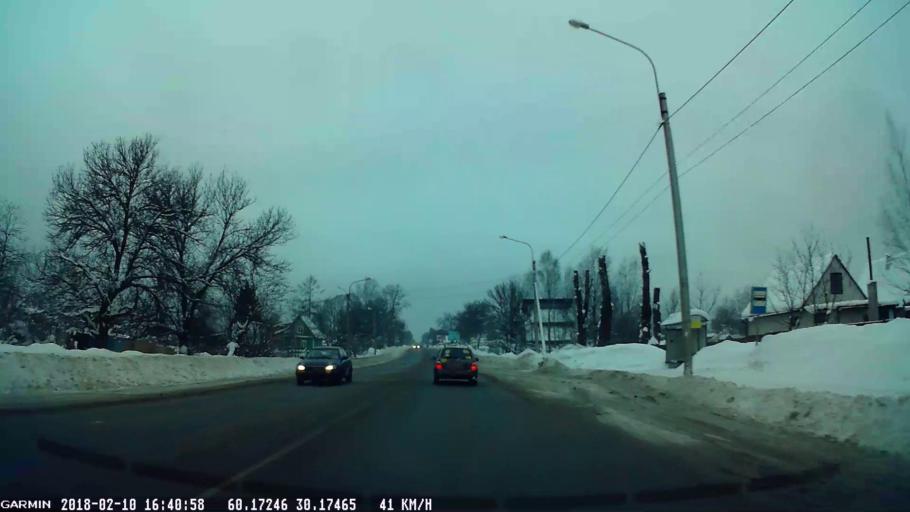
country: RU
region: Leningrad
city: Sertolovo
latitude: 60.1626
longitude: 30.1831
